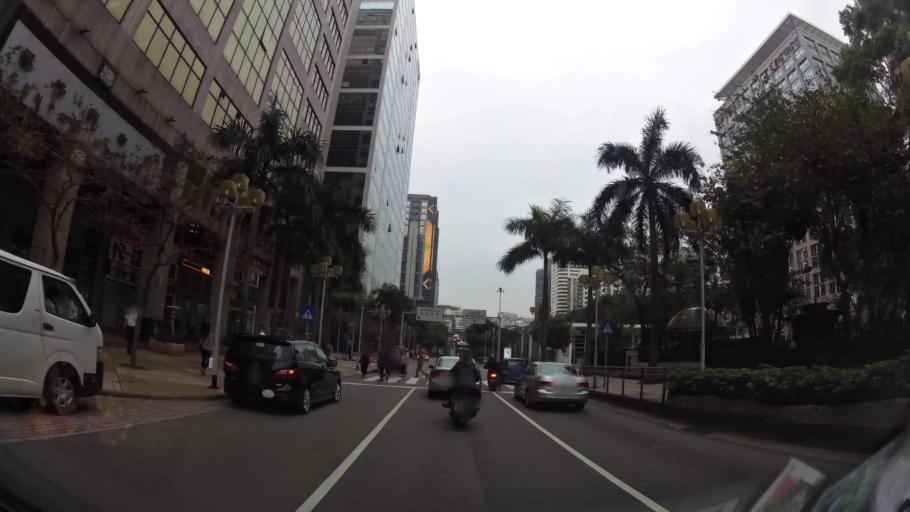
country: MO
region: Macau
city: Macau
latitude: 22.1895
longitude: 113.5502
